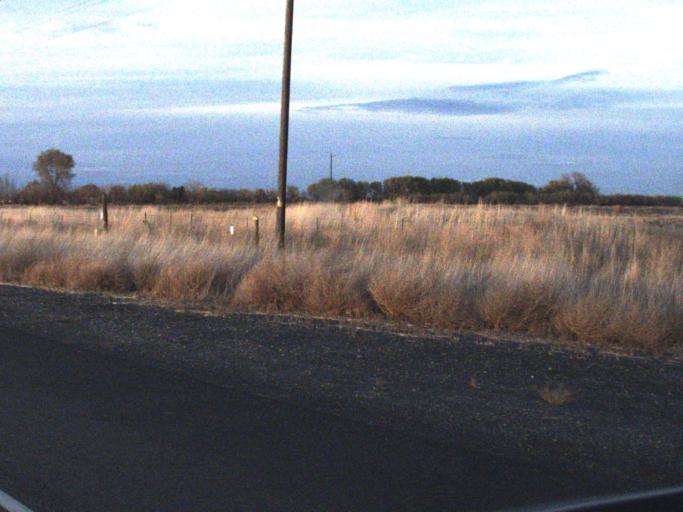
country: US
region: Washington
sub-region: Walla Walla County
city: Burbank
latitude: 46.1862
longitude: -118.9796
